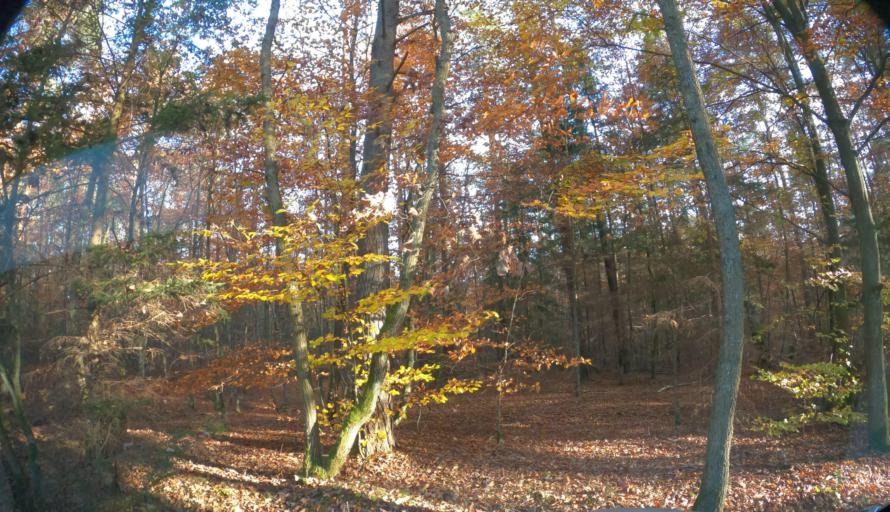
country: PL
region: Greater Poland Voivodeship
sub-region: Powiat zlotowski
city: Okonek
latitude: 53.5319
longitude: 16.9081
